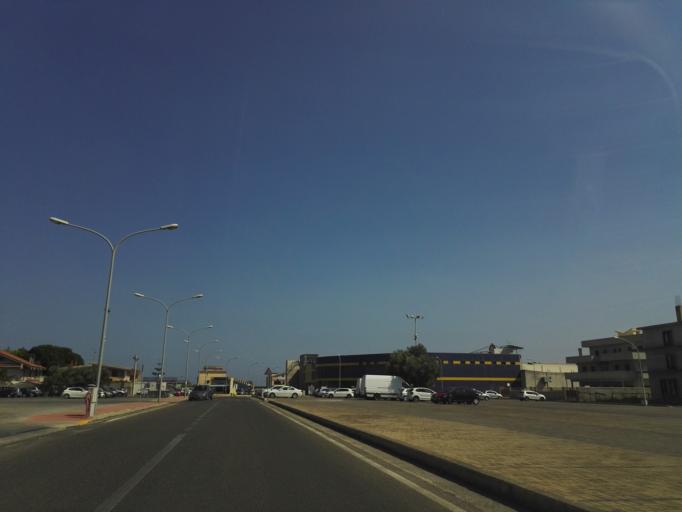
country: IT
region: Calabria
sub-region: Provincia di Reggio Calabria
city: Marina di Gioiosa Ionica
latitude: 38.2901
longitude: 16.3139
